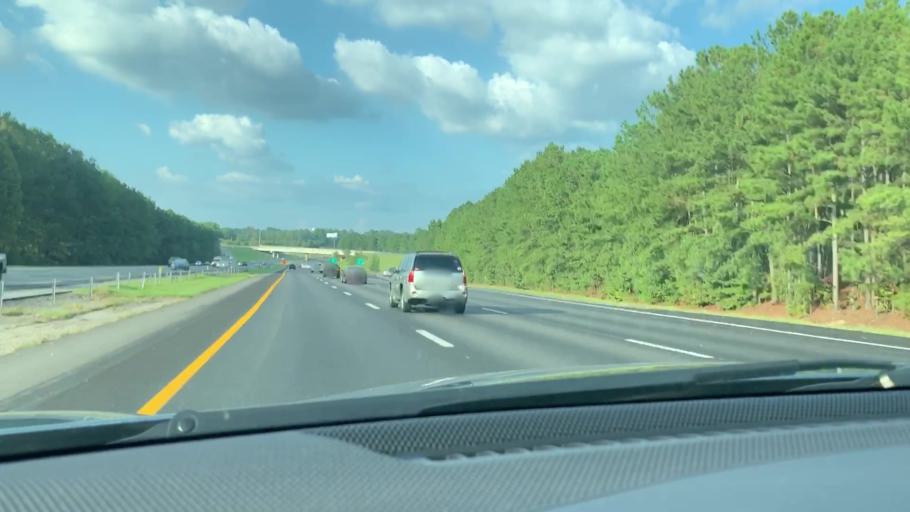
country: US
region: South Carolina
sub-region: Richland County
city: Woodfield
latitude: 34.0355
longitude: -80.9381
